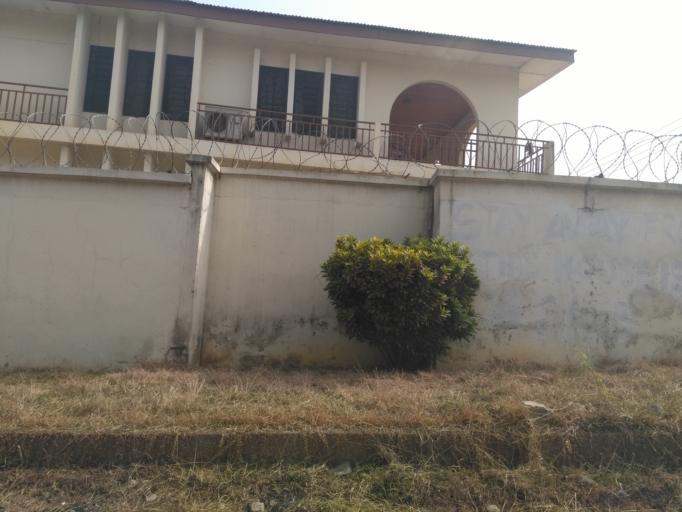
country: GH
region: Ashanti
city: Kumasi
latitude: 6.6762
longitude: -1.6050
